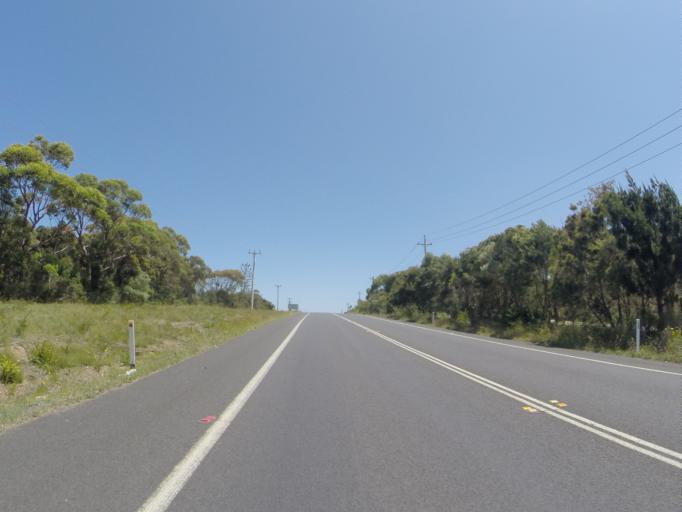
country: AU
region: New South Wales
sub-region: Shoalhaven Shire
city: Ulladulla
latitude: -35.3747
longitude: 150.4621
